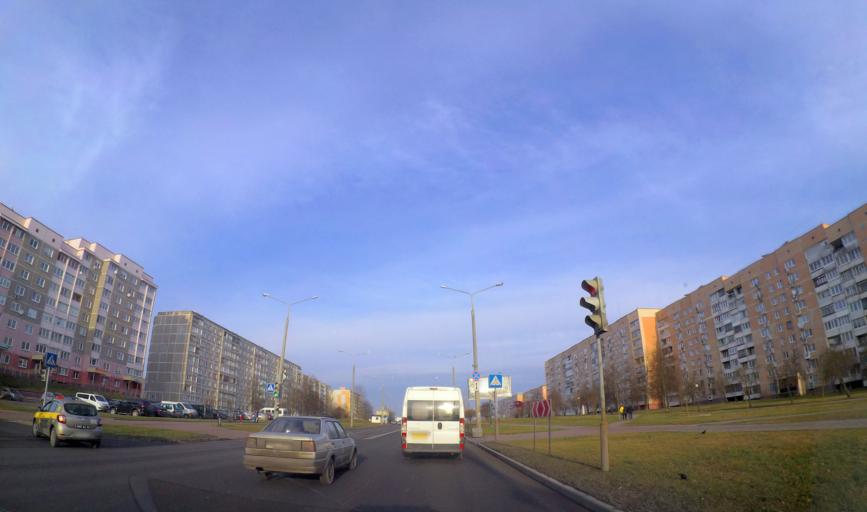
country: BY
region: Grodnenskaya
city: Hrodna
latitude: 53.6614
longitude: 23.7829
